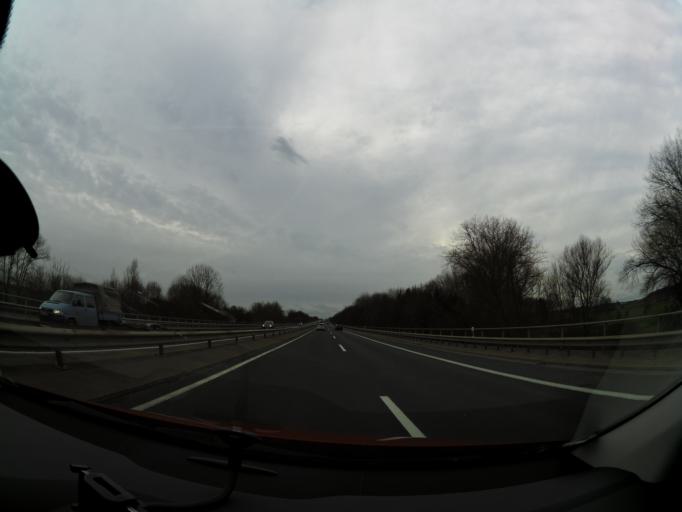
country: DE
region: Lower Saxony
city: Leiferde
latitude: 52.1918
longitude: 10.5201
